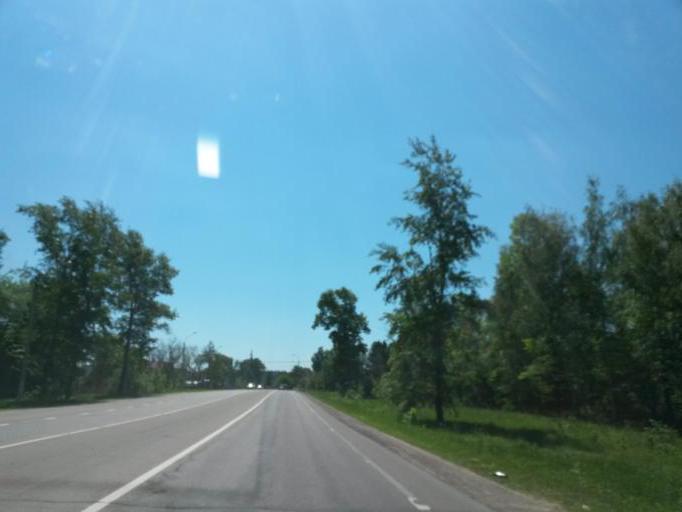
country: RU
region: Moskovskaya
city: Stolbovaya
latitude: 55.2079
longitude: 37.5069
